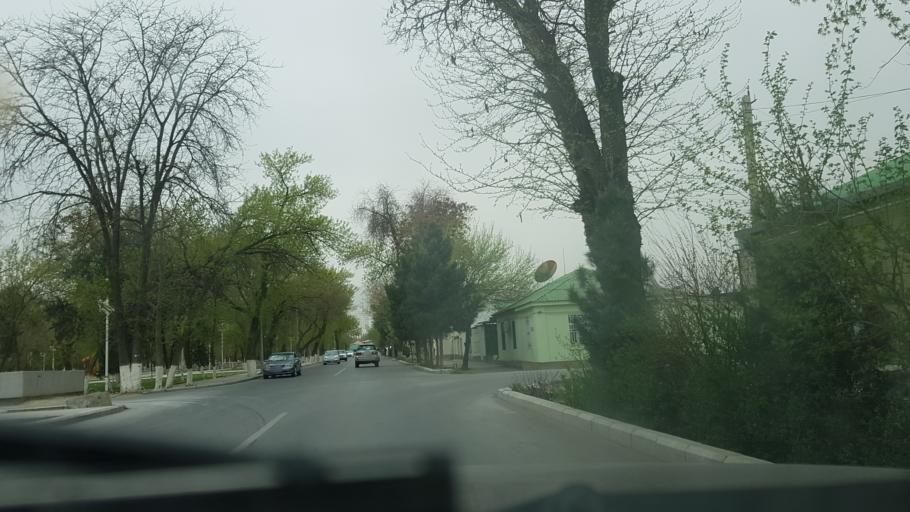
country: TM
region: Ahal
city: Ashgabat
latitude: 37.9519
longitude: 58.3633
